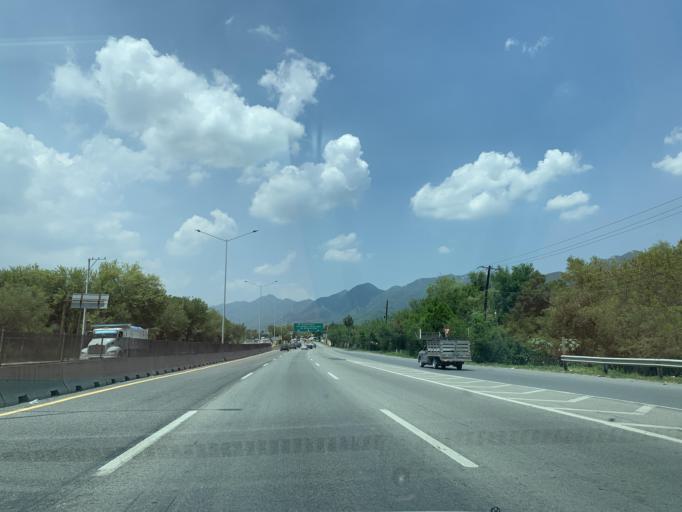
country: MX
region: Nuevo Leon
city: Santiago
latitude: 25.4354
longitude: -100.1530
